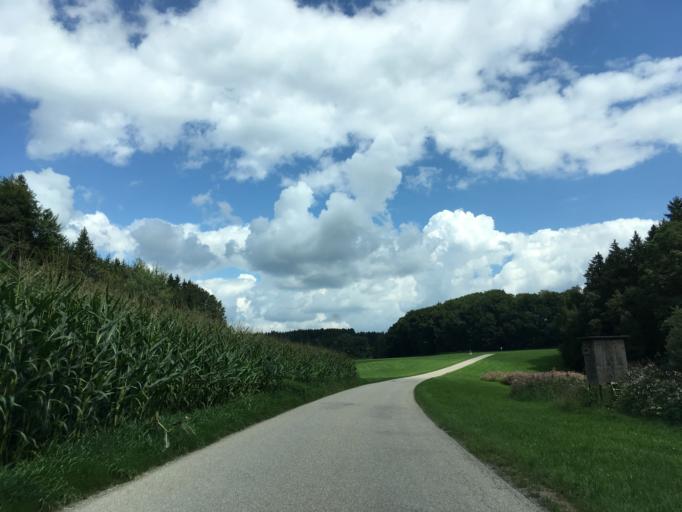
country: DE
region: Bavaria
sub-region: Upper Bavaria
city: Schnaitsee
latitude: 48.0604
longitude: 12.3359
